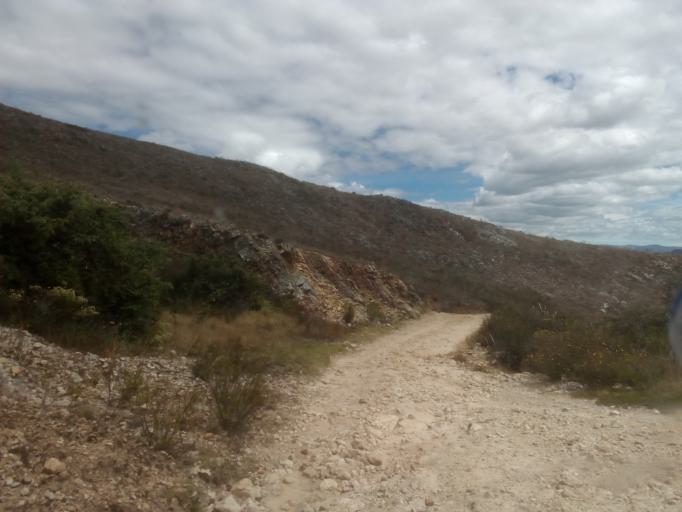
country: PE
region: La Libertad
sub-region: Sanchez Carrion
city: Curgos
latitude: -7.8002
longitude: -77.9745
